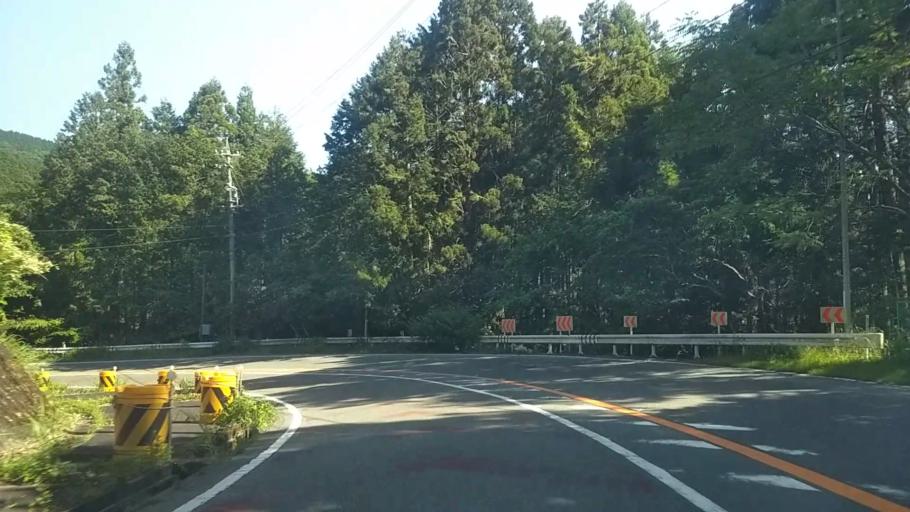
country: JP
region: Shizuoka
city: Fujinomiya
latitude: 35.1869
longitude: 138.5291
